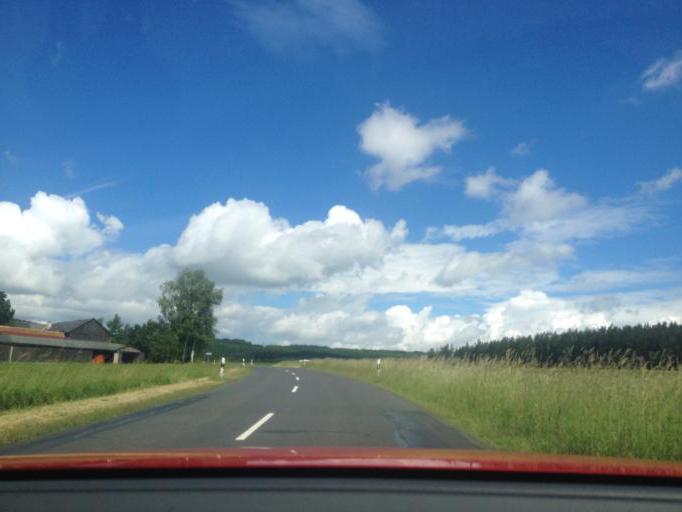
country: DE
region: Bavaria
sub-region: Upper Palatinate
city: Pechbrunn
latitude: 49.9762
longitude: 12.1779
